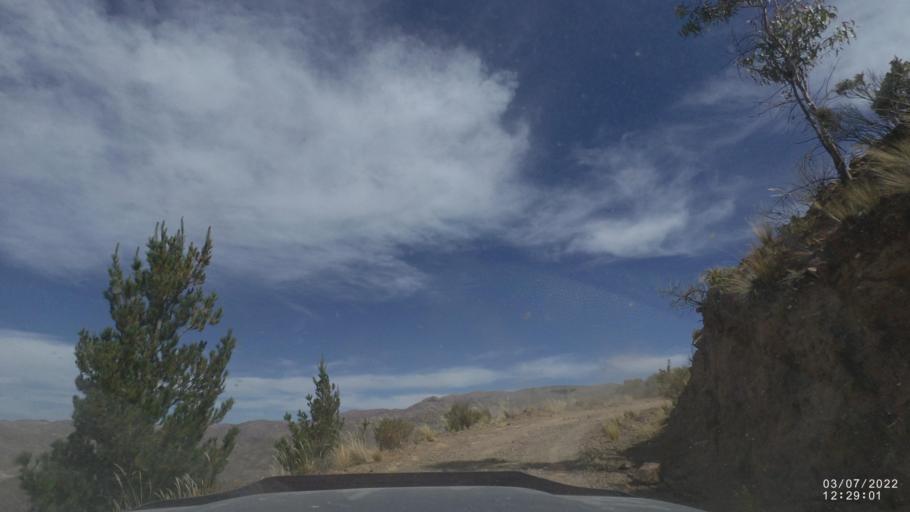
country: BO
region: Cochabamba
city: Irpa Irpa
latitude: -17.8117
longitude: -66.6117
